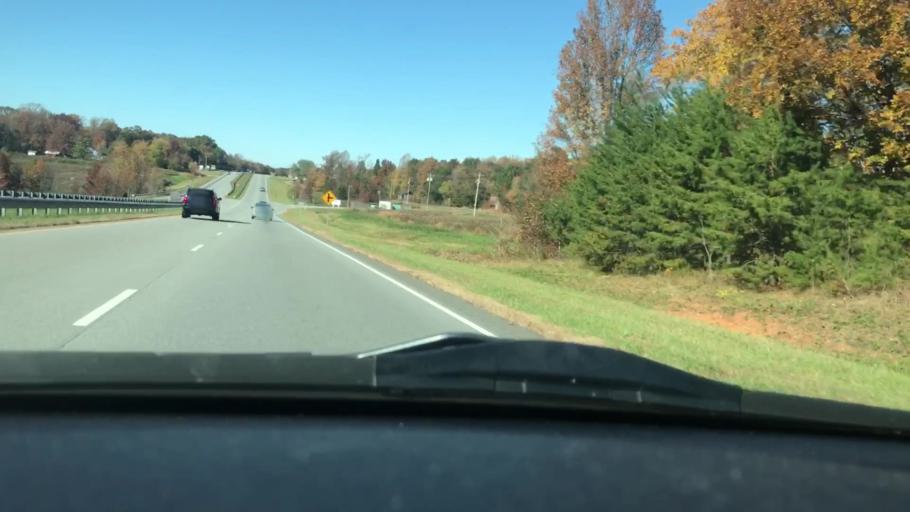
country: US
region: North Carolina
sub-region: Rockingham County
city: Madison
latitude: 36.3191
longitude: -79.9441
